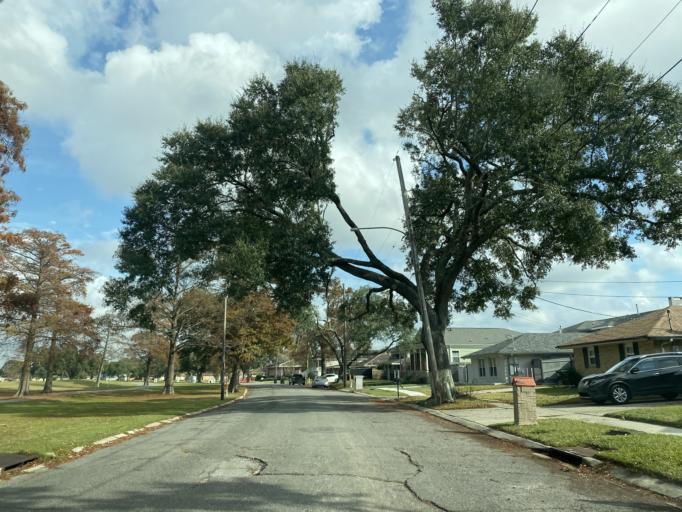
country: US
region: Louisiana
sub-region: Orleans Parish
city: New Orleans
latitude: 30.0173
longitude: -90.0405
